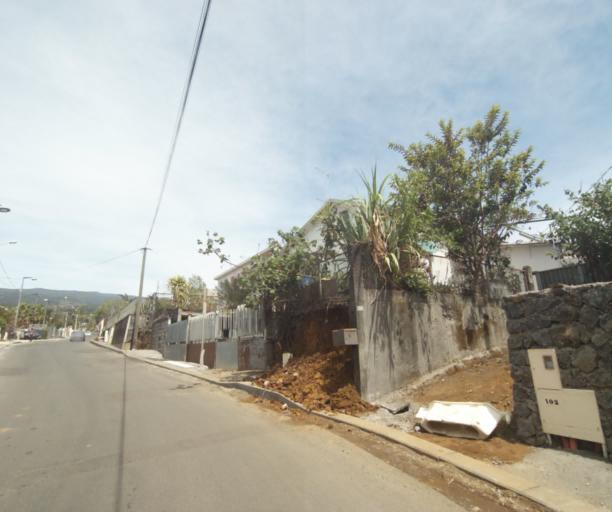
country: RE
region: Reunion
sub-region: Reunion
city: Saint-Paul
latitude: -21.0393
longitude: 55.2986
